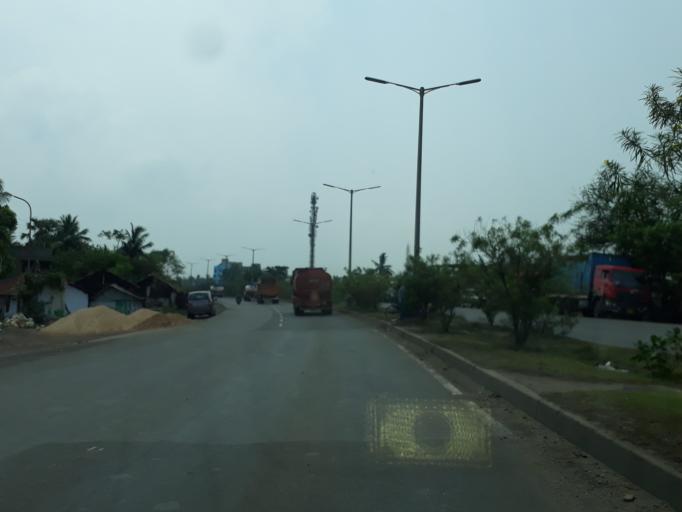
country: IN
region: West Bengal
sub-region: Purba Medinipur
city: Haldia
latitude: 22.0647
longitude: 88.0806
